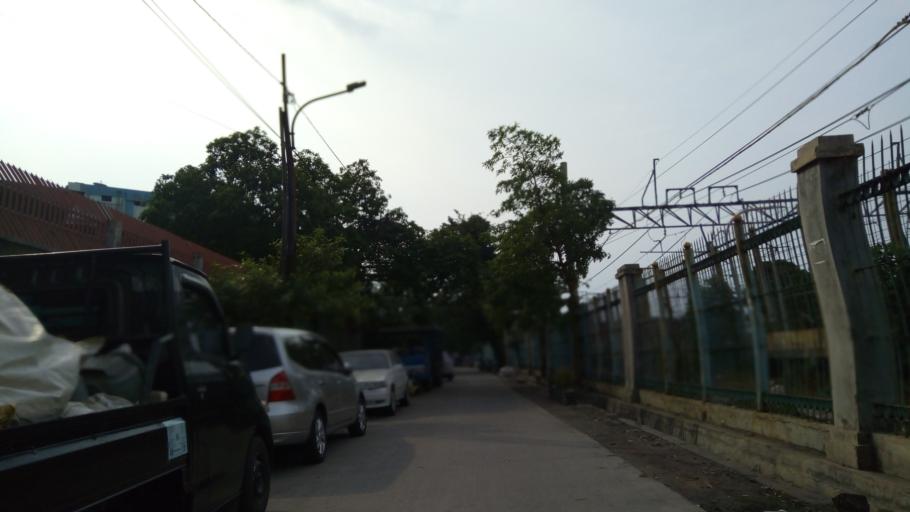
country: ID
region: Jakarta Raya
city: Jakarta
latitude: -6.1465
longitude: 106.8371
